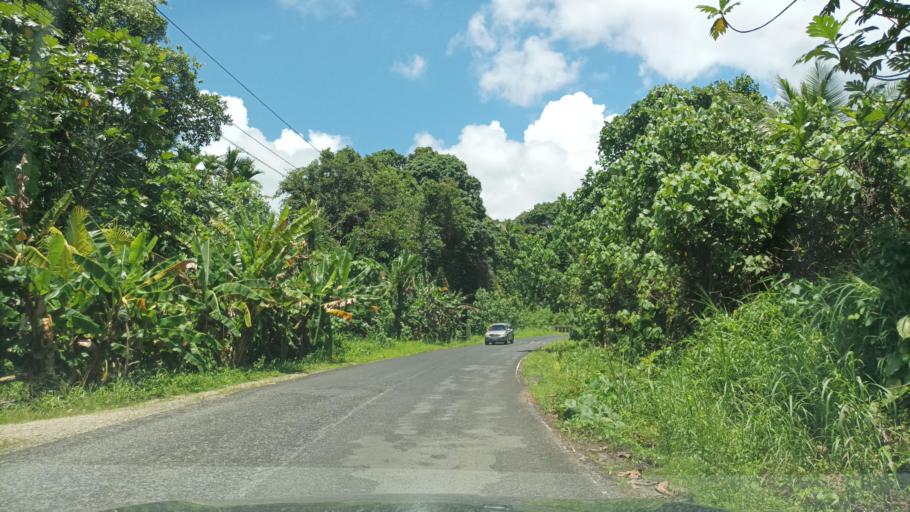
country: FM
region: Pohnpei
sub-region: Madolenihm Municipality
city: Madolenihm Municipality Government
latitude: 6.8743
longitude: 158.2873
